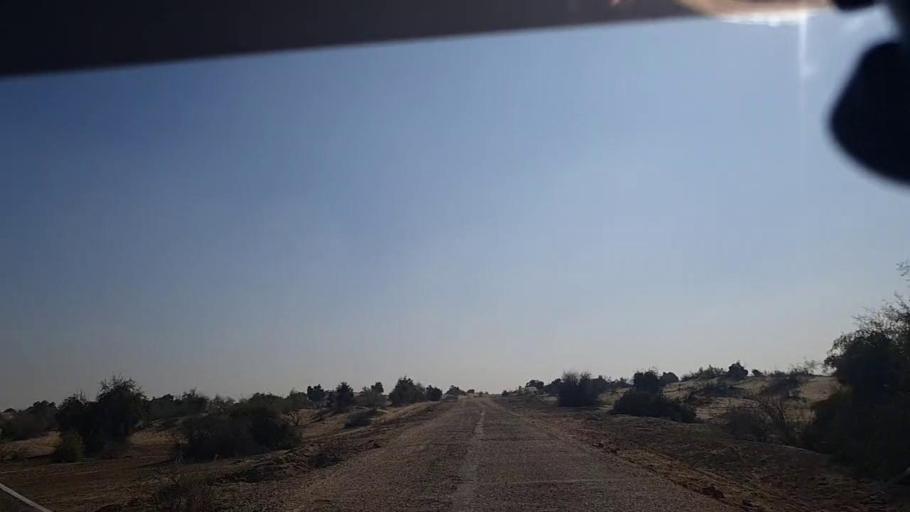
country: PK
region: Sindh
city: Khanpur
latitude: 27.5769
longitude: 69.3054
